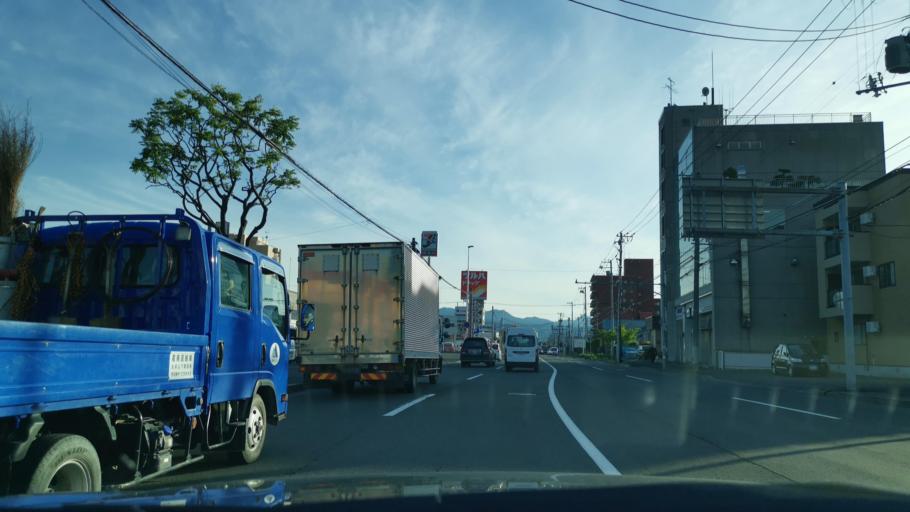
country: JP
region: Hokkaido
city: Sapporo
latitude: 43.0677
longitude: 141.4008
